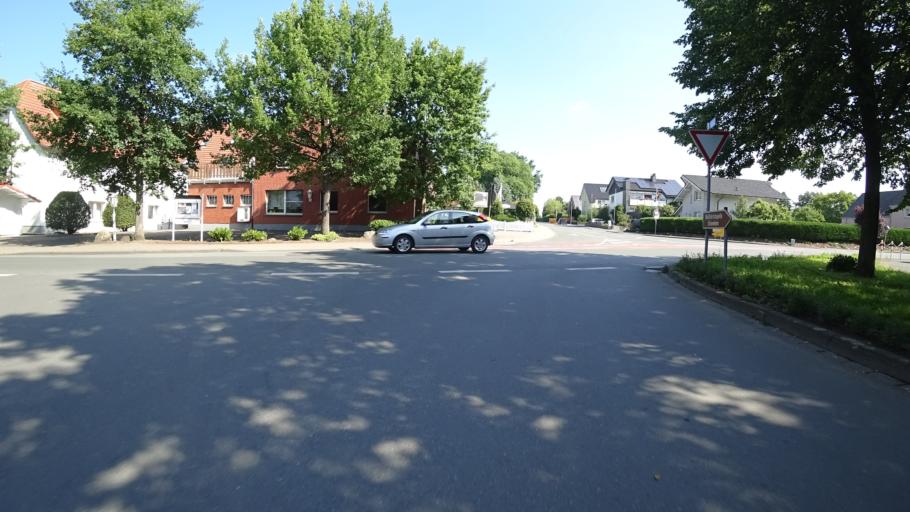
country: DE
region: North Rhine-Westphalia
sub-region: Regierungsbezirk Arnsberg
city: Lippstadt
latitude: 51.6676
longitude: 8.3827
